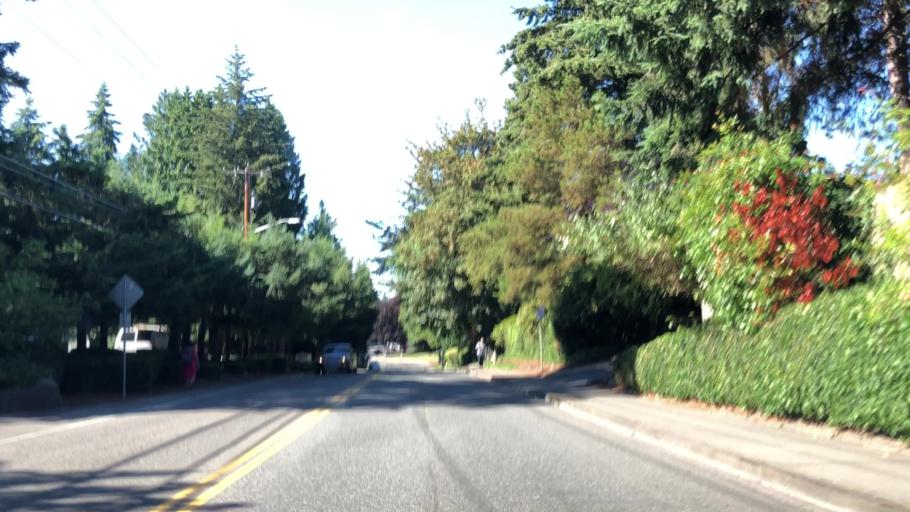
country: US
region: Washington
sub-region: King County
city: Kirkland
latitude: 47.7079
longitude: -122.2079
